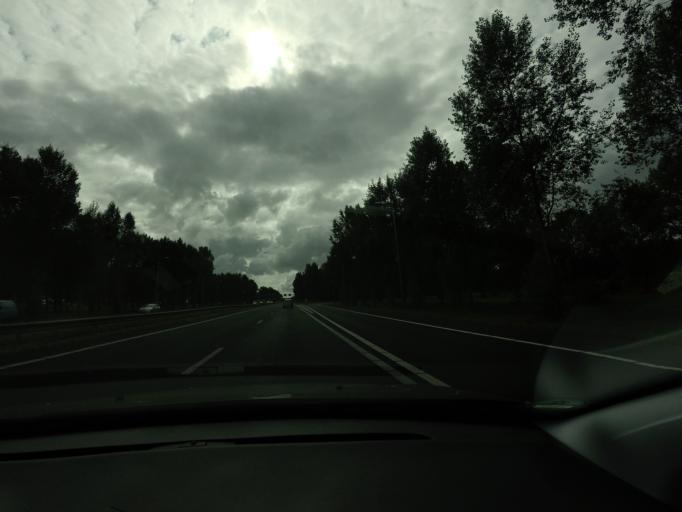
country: NL
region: North Holland
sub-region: Gemeente Hoorn
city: Hoorn
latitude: 52.6932
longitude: 5.0300
